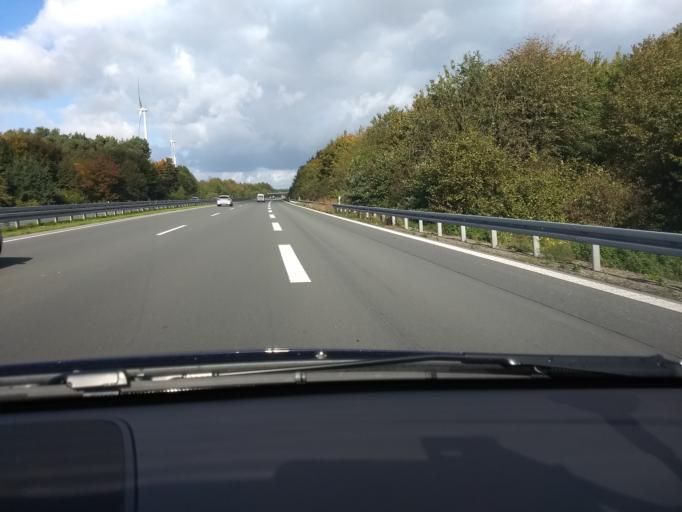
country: DE
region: North Rhine-Westphalia
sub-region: Regierungsbezirk Munster
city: Heiden
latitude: 51.7796
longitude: 6.9670
